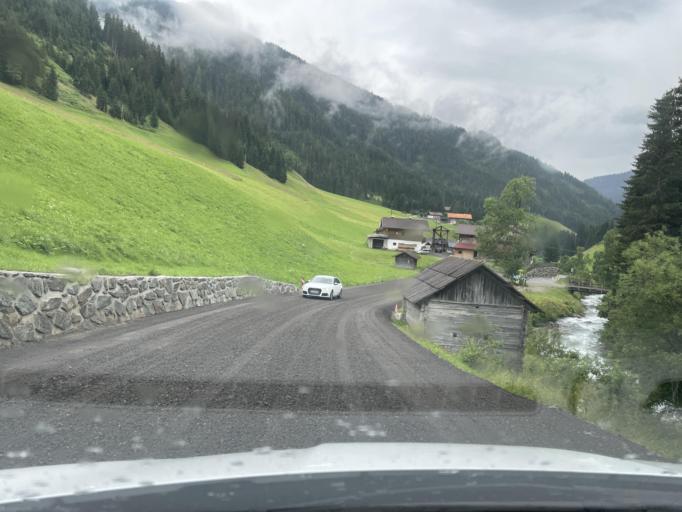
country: AT
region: Tyrol
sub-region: Politischer Bezirk Lienz
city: Ausservillgraten
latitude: 46.7986
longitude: 12.4478
